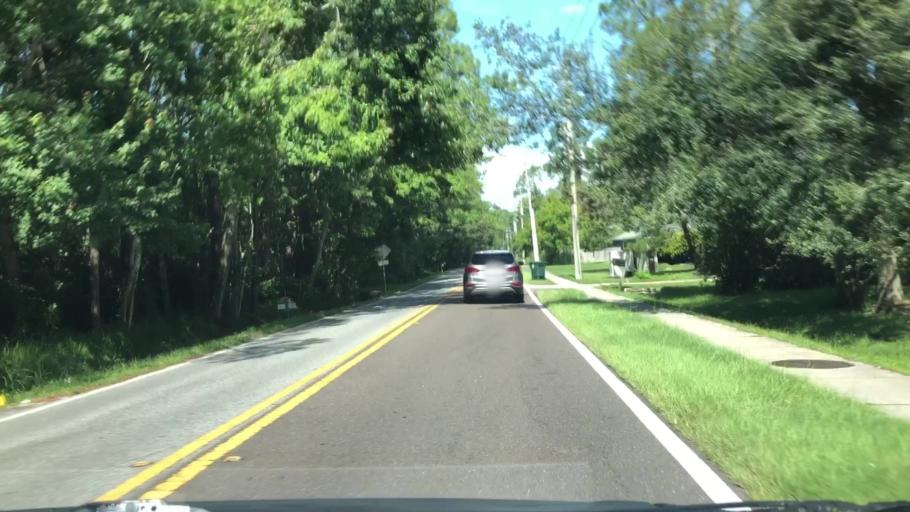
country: US
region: Florida
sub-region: Saint Johns County
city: Fruit Cove
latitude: 30.1848
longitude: -81.6143
